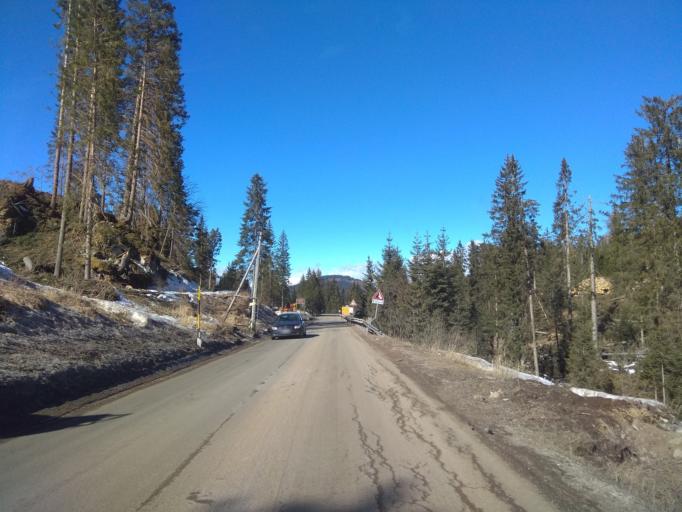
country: IT
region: Trentino-Alto Adige
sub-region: Bolzano
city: Nova Levante
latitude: 46.4105
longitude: 11.5800
